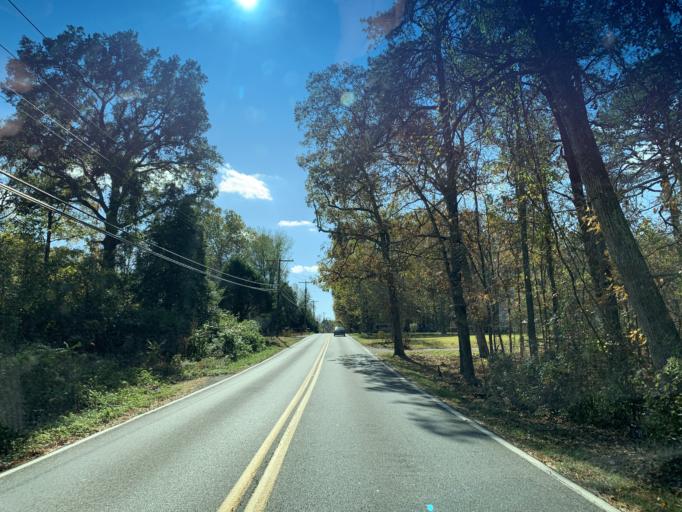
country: US
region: Maryland
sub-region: Anne Arundel County
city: Gambrills
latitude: 39.0963
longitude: -76.6533
